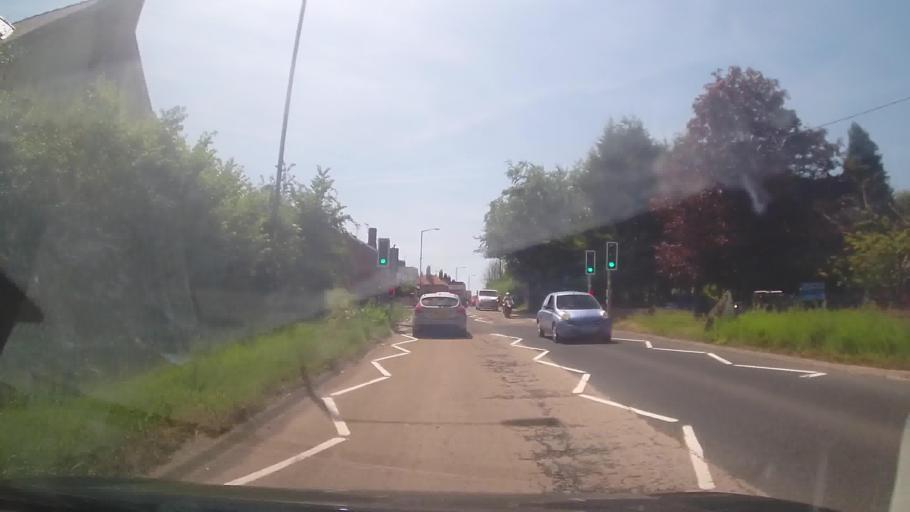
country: GB
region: England
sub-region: Herefordshire
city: Hereford
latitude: 52.0773
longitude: -2.7224
